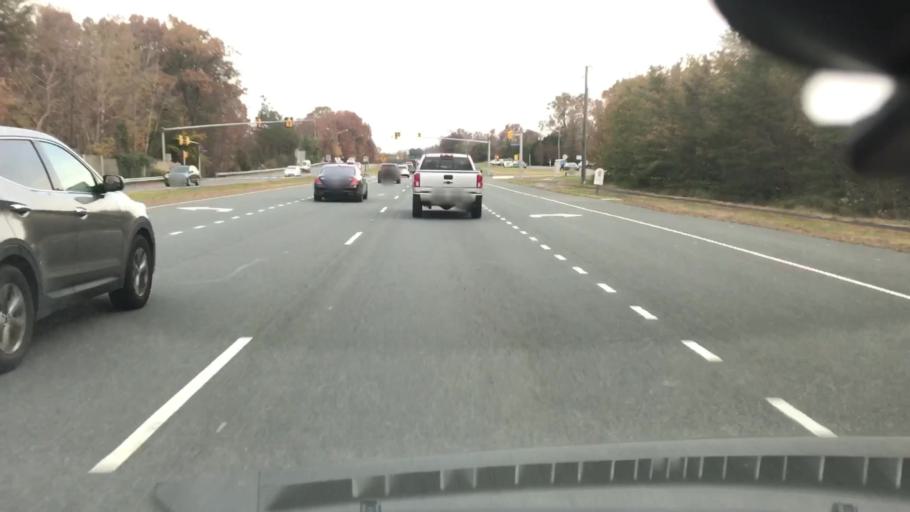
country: US
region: Virginia
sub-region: Fairfax County
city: Fairfax Station
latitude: 38.7942
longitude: -77.3258
